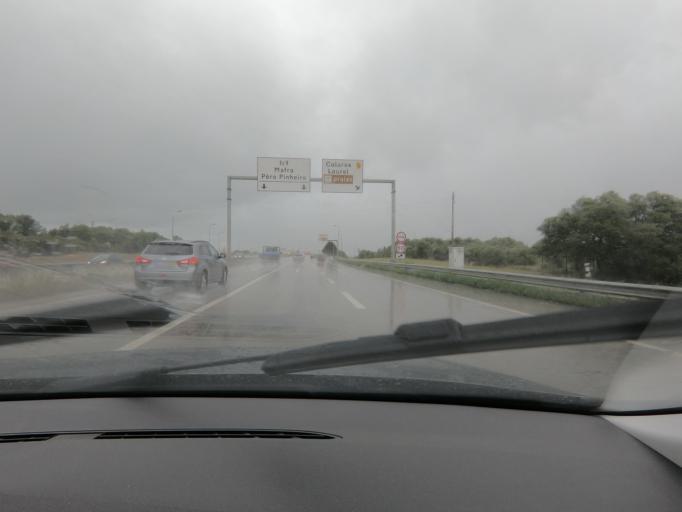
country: PT
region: Lisbon
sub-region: Sintra
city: Sintra
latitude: 38.8150
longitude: -9.3589
